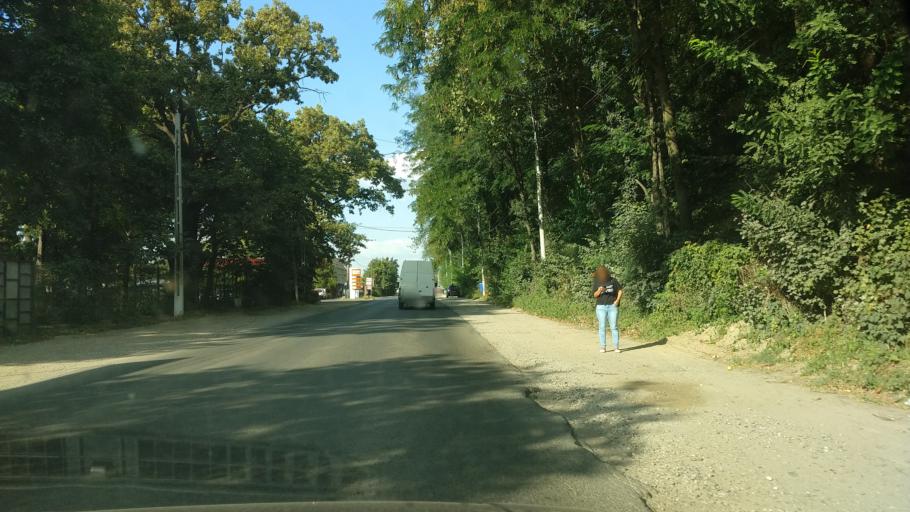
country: RO
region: Ilfov
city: Stefanestii de Jos
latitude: 44.5206
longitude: 26.1941
